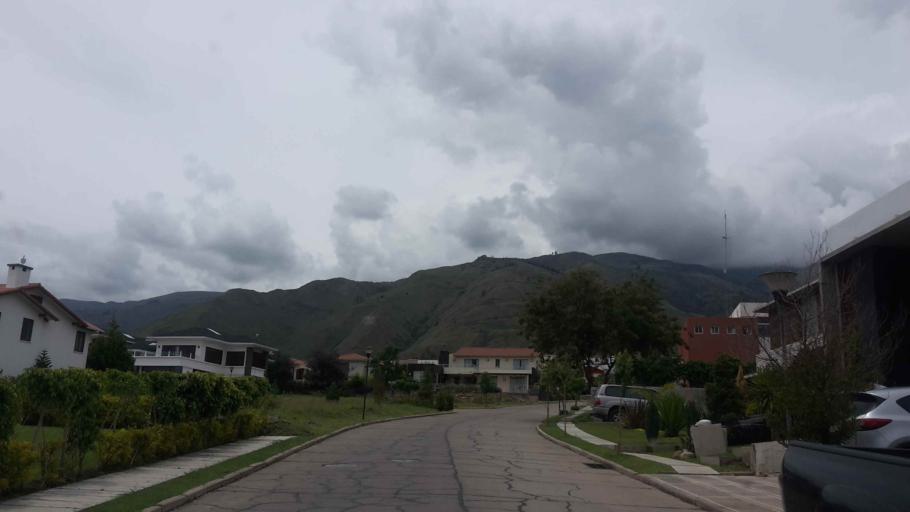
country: BO
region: Cochabamba
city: Cochabamba
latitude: -17.3415
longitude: -66.1842
